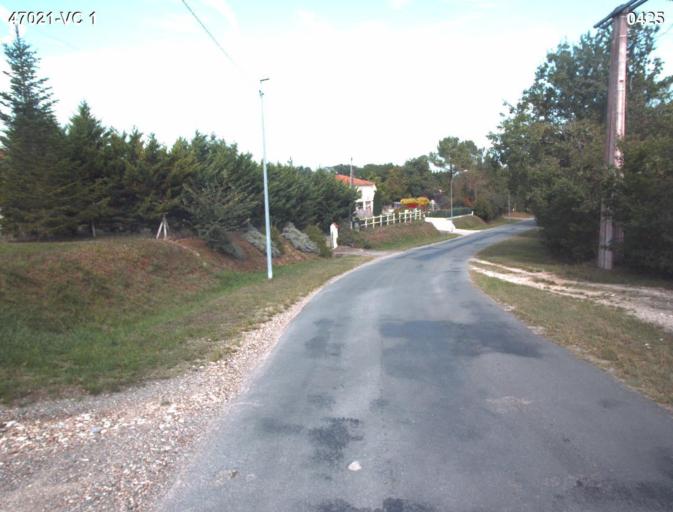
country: FR
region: Aquitaine
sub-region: Departement du Lot-et-Garonne
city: Barbaste
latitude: 44.1624
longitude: 0.2862
